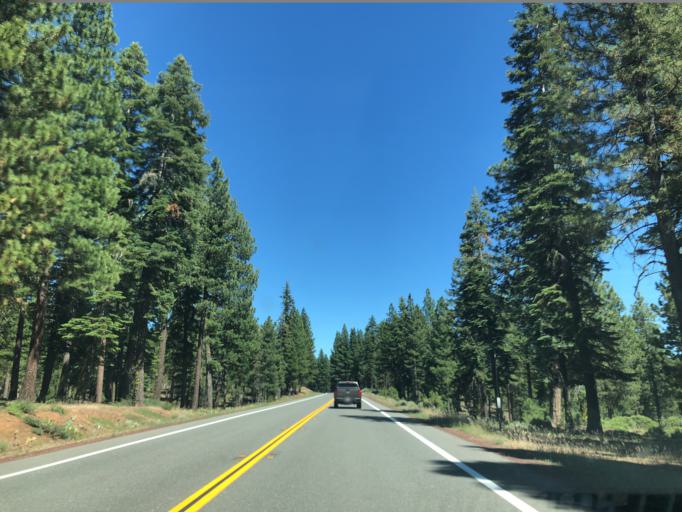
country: US
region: California
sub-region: Lassen County
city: Westwood
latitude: 40.4402
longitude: -120.8563
